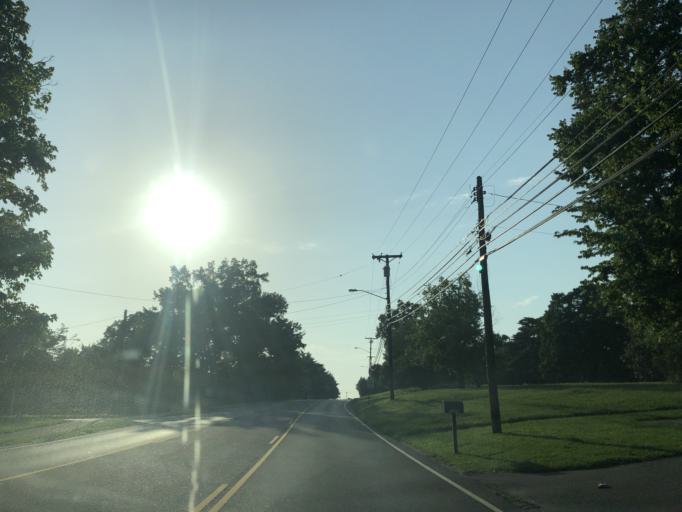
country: US
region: Tennessee
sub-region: Davidson County
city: Lakewood
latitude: 36.1449
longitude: -86.6579
